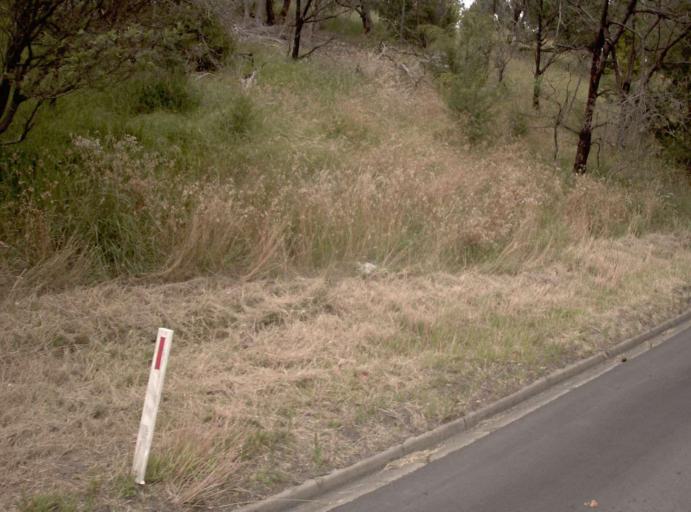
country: AU
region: Victoria
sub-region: Latrobe
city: Traralgon
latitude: -38.2469
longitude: 146.5245
